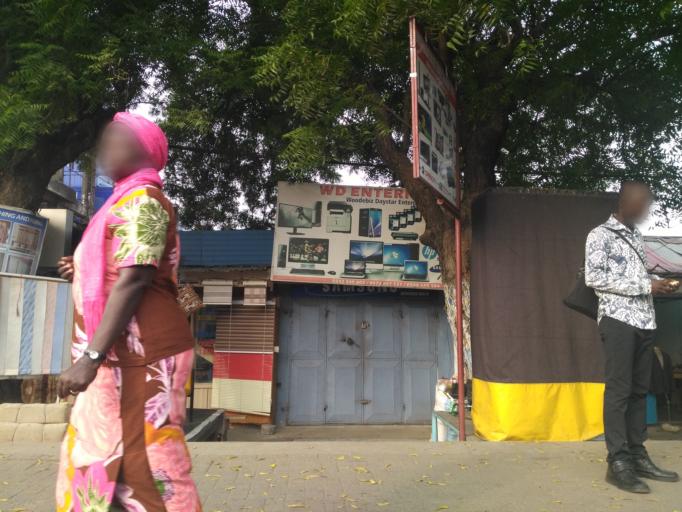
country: GH
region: Greater Accra
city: Accra
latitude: 5.5587
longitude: -0.2127
